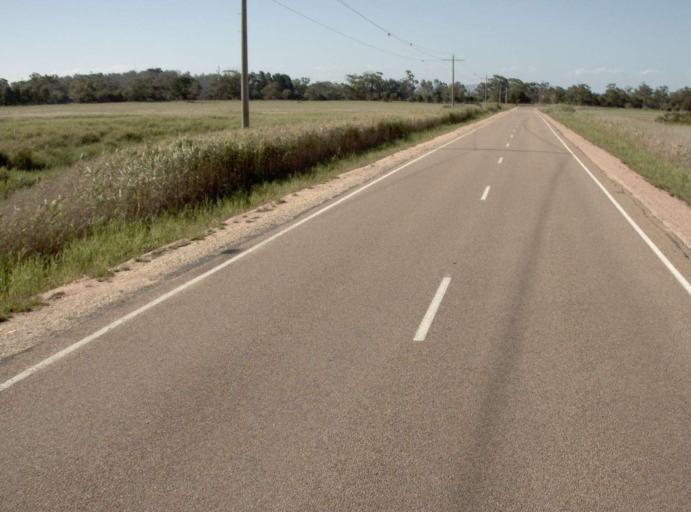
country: AU
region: Victoria
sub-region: East Gippsland
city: Lakes Entrance
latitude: -37.7740
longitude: 148.5378
